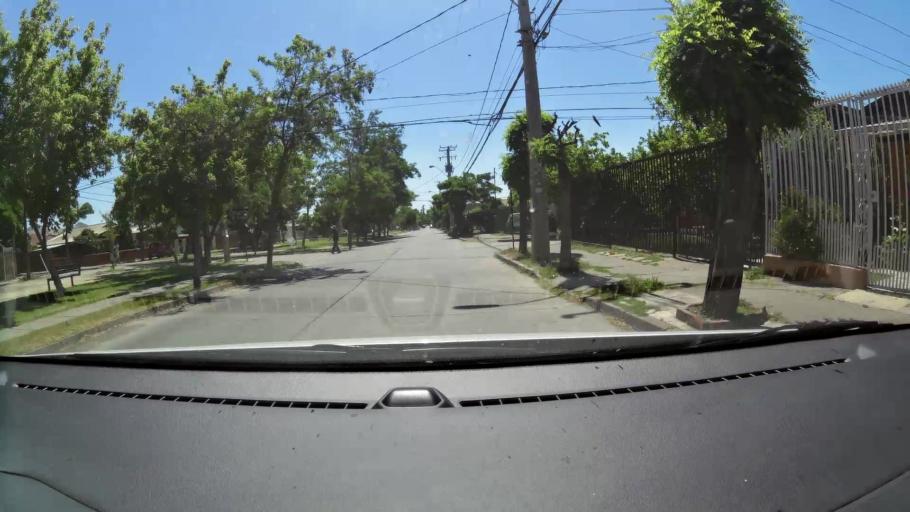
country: CL
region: Santiago Metropolitan
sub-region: Provincia de Maipo
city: San Bernardo
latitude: -33.5702
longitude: -70.6813
